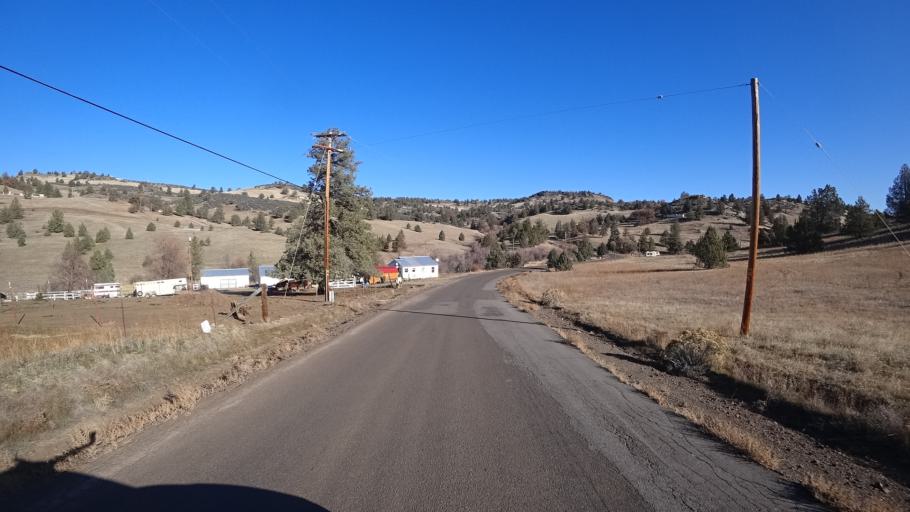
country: US
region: California
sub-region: Siskiyou County
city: Montague
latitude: 41.8933
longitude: -122.4260
